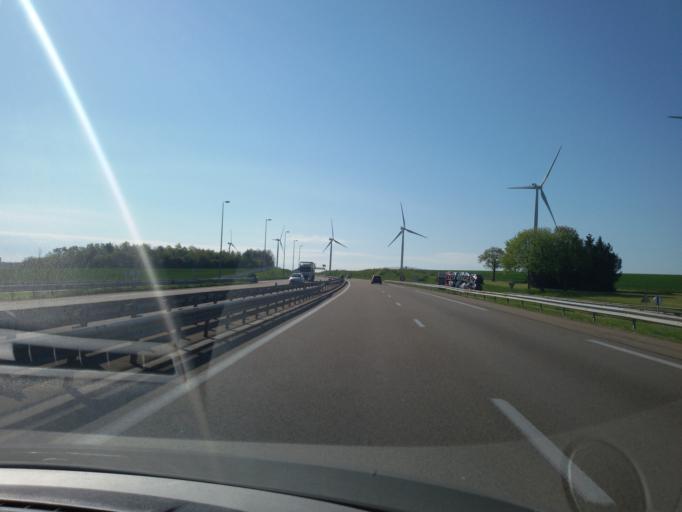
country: FR
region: Bourgogne
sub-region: Departement de l'Yonne
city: Venoy
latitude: 47.7875
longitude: 3.6729
